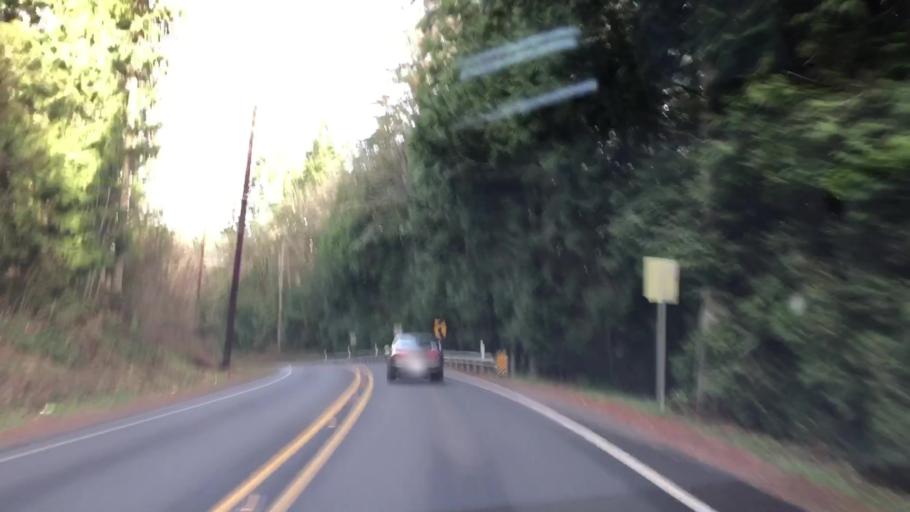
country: US
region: Washington
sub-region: Kitsap County
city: Indianola
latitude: 47.7865
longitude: -122.5419
